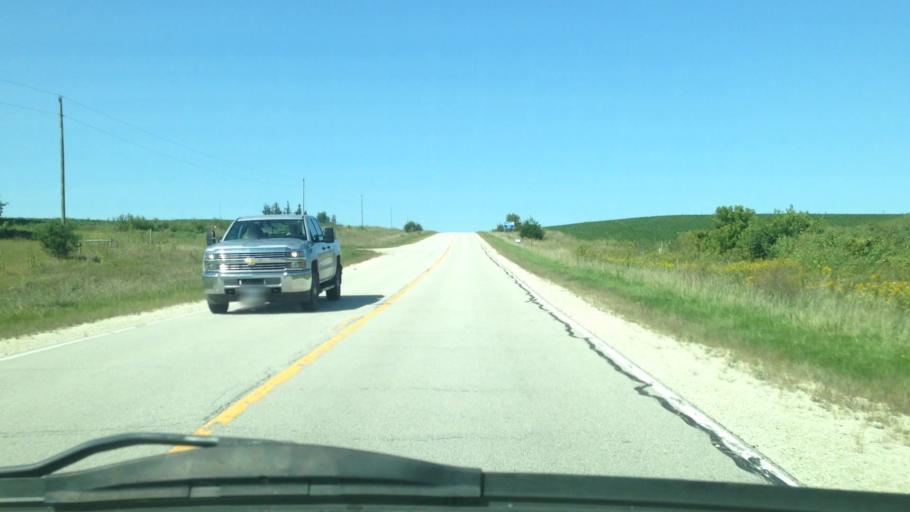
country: US
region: Minnesota
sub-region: Houston County
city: Spring Grove
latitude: 43.6335
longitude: -91.7903
